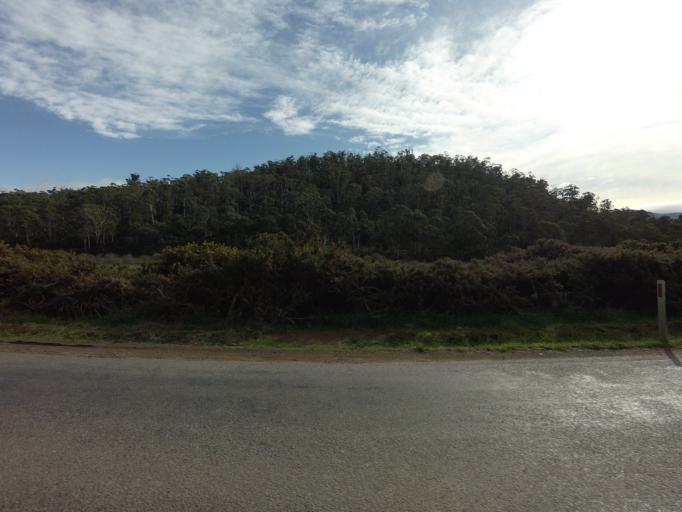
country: AU
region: Tasmania
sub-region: Derwent Valley
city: New Norfolk
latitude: -42.7809
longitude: 147.0091
